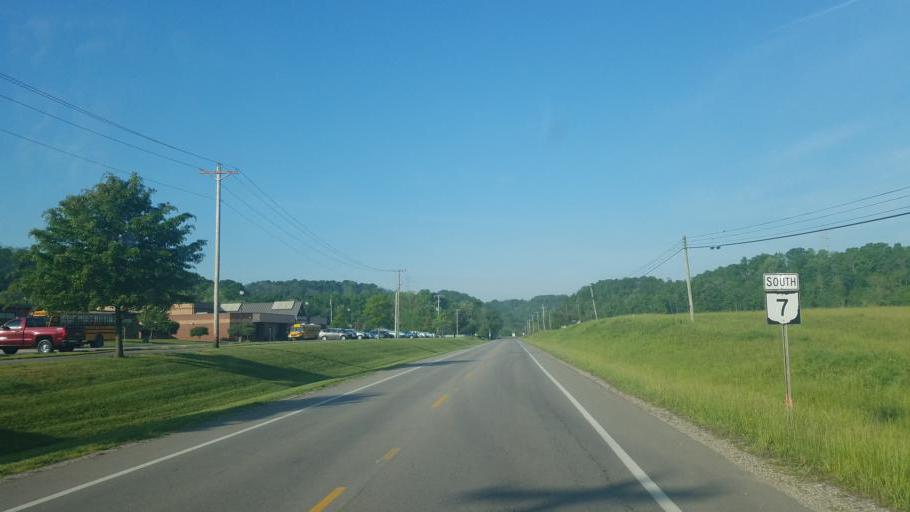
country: US
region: West Virginia
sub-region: Mason County
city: New Haven
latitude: 39.1230
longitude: -81.8831
